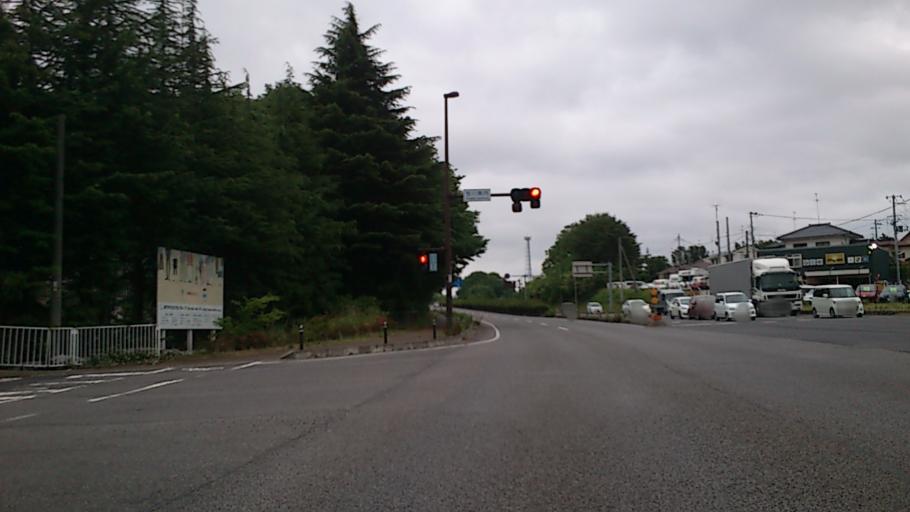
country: JP
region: Fukushima
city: Koriyama
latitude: 37.3446
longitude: 140.3578
